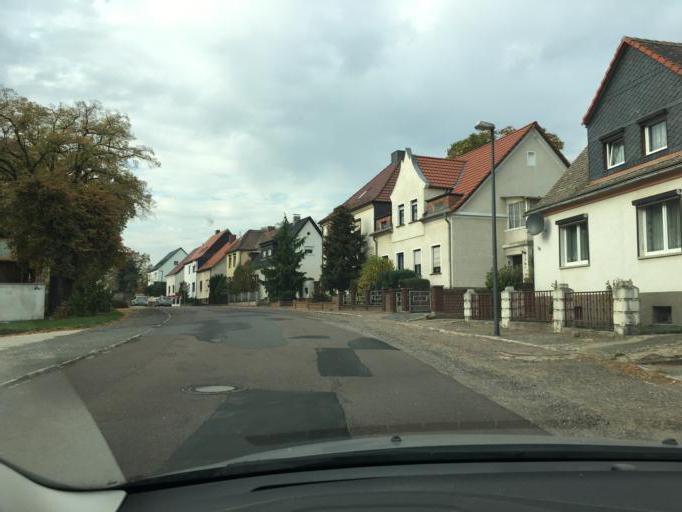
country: DE
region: Saxony-Anhalt
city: Landsberg
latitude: 51.5240
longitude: 12.1658
